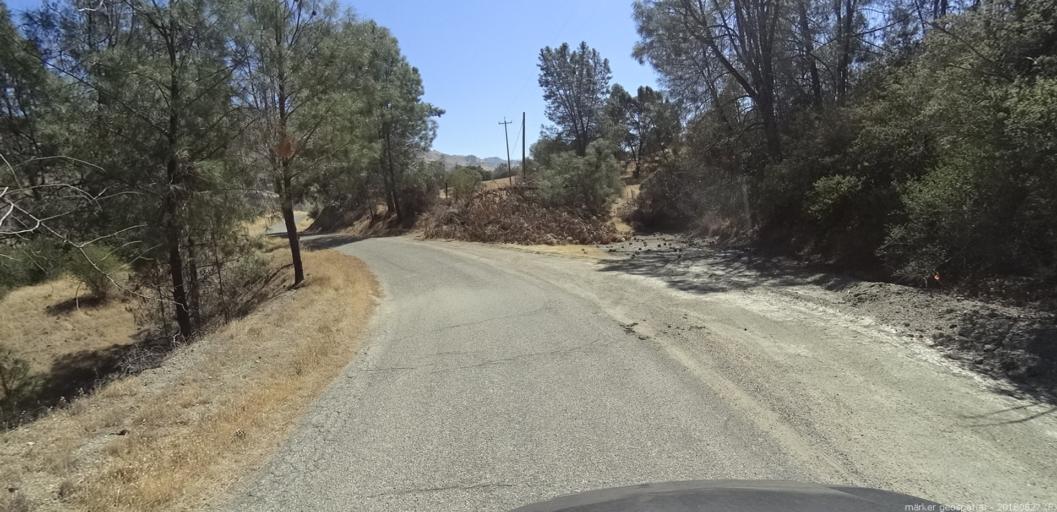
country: US
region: California
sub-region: Monterey County
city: King City
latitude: 36.2925
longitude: -120.8752
